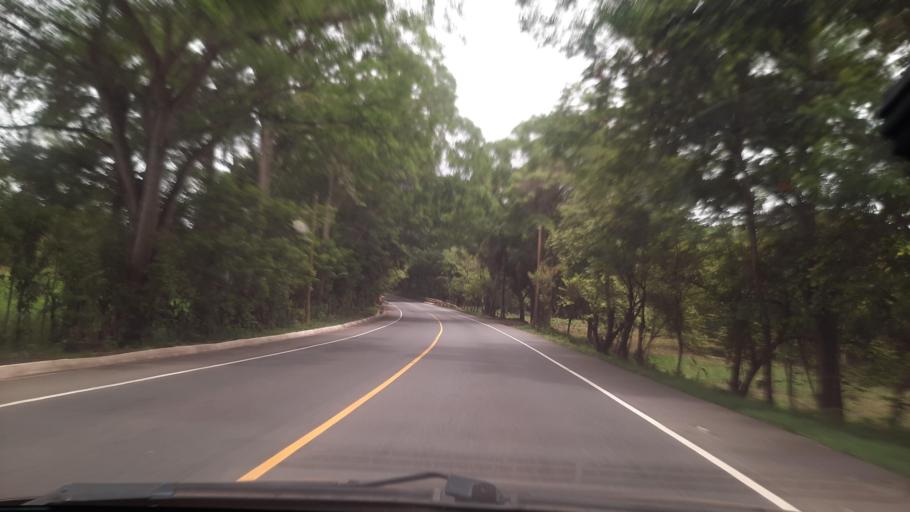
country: GT
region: Izabal
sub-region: Municipio de Los Amates
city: Los Amates
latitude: 15.2403
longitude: -89.1772
